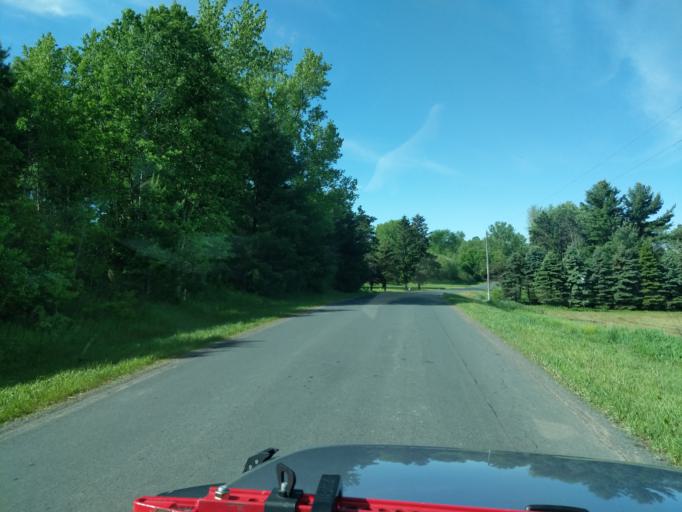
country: US
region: Wisconsin
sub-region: Pierce County
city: River Falls
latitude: 44.8672
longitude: -92.5147
